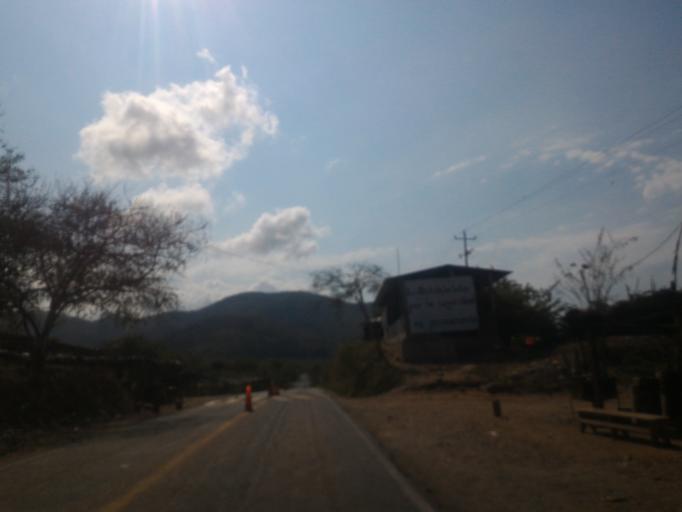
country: MX
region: Michoacan
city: Coahuayana Viejo
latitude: 18.5072
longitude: -103.5757
